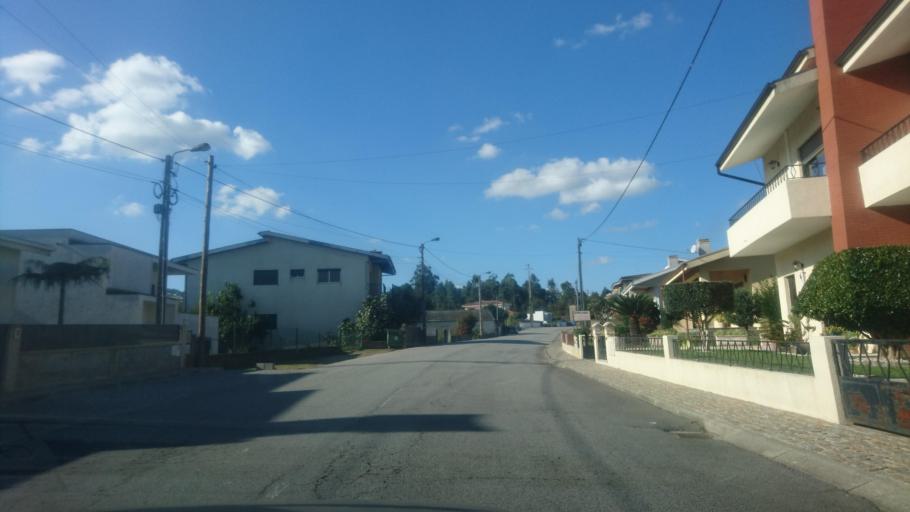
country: PT
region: Porto
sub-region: Paredes
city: Madalena
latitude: 41.2187
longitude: -8.3368
